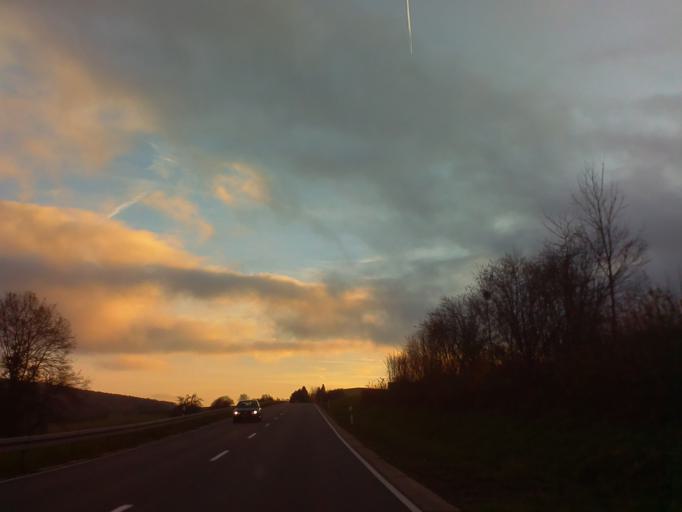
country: DE
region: Hesse
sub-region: Regierungsbezirk Darmstadt
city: Beerfelden
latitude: 49.5823
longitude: 8.9845
